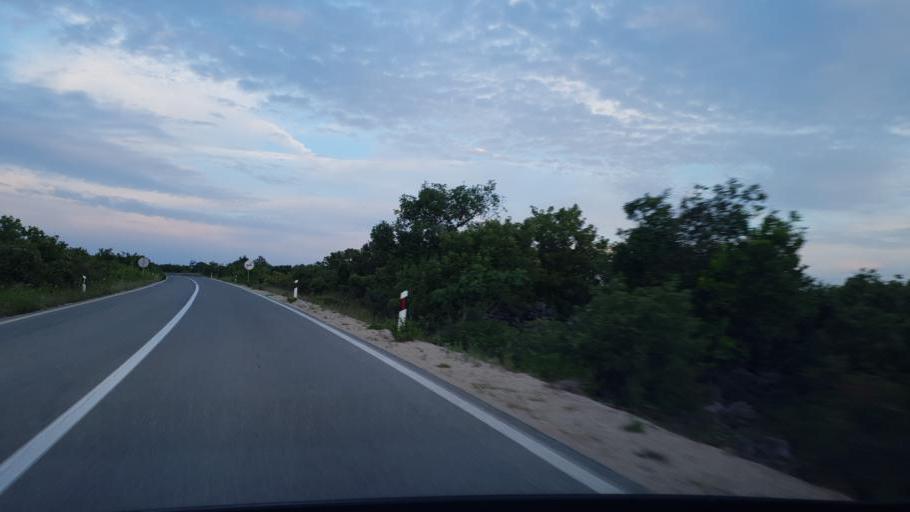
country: HR
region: Primorsko-Goranska
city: Punat
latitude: 45.0373
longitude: 14.6472
